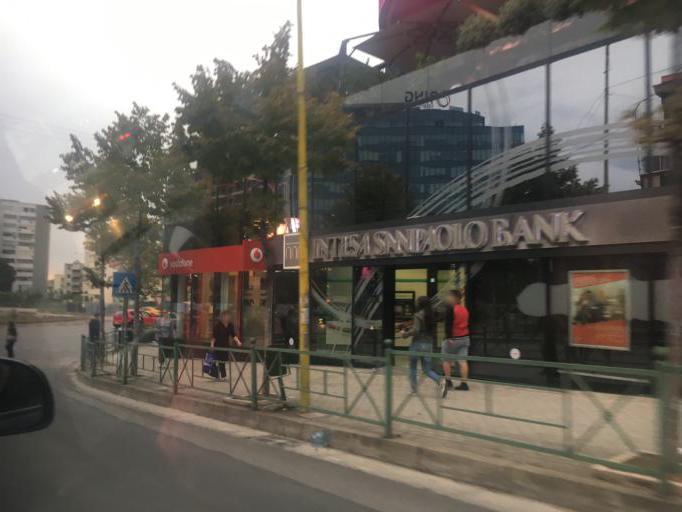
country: AL
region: Tirane
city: Tirana
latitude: 41.3328
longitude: 19.8053
